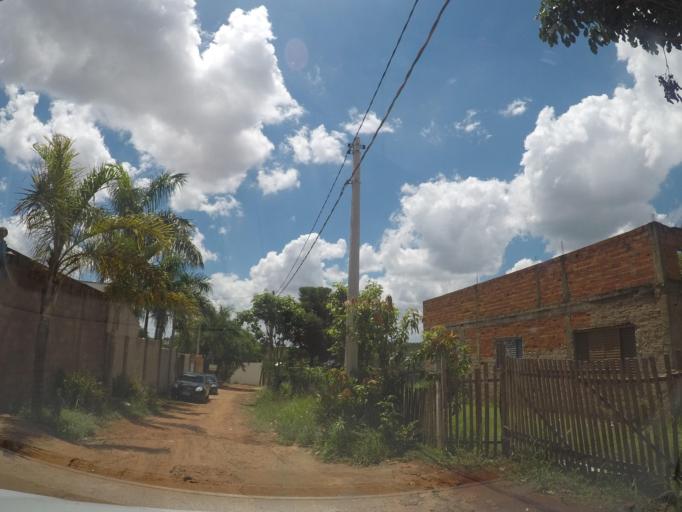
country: BR
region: Sao Paulo
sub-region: Hortolandia
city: Hortolandia
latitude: -22.8383
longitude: -47.2388
